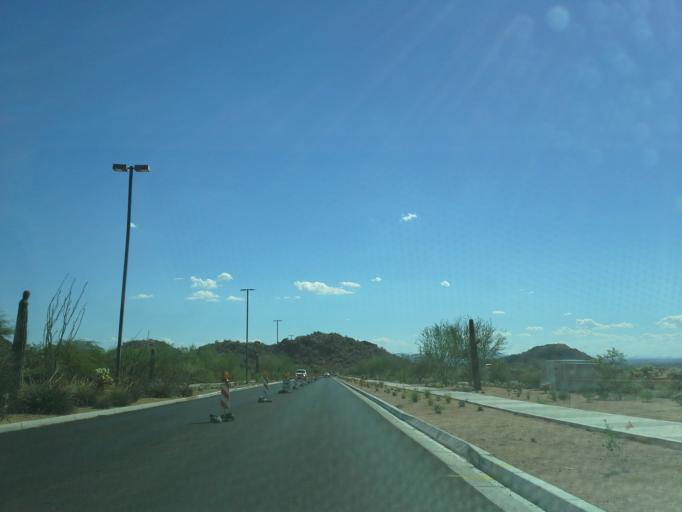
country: US
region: Arizona
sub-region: Pinal County
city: Apache Junction
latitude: 33.4583
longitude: -111.6325
